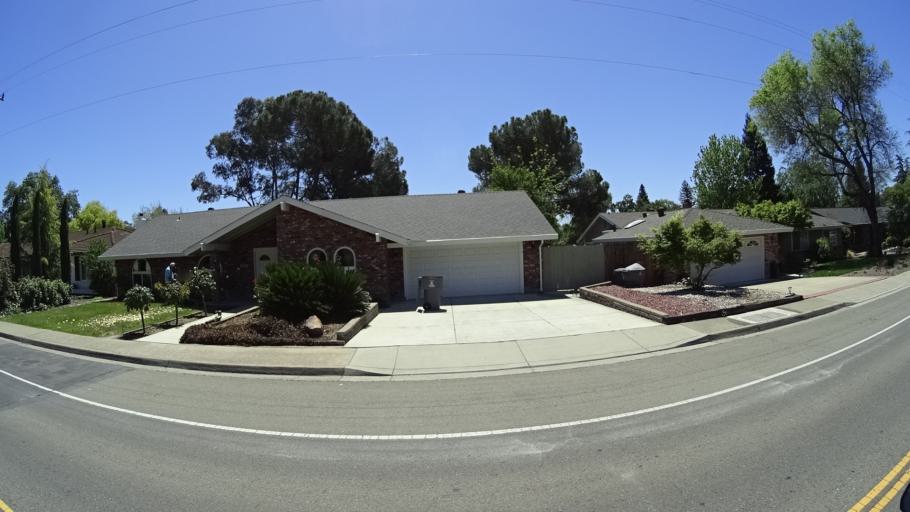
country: US
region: California
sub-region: Placer County
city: Rocklin
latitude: 38.7981
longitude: -121.2436
